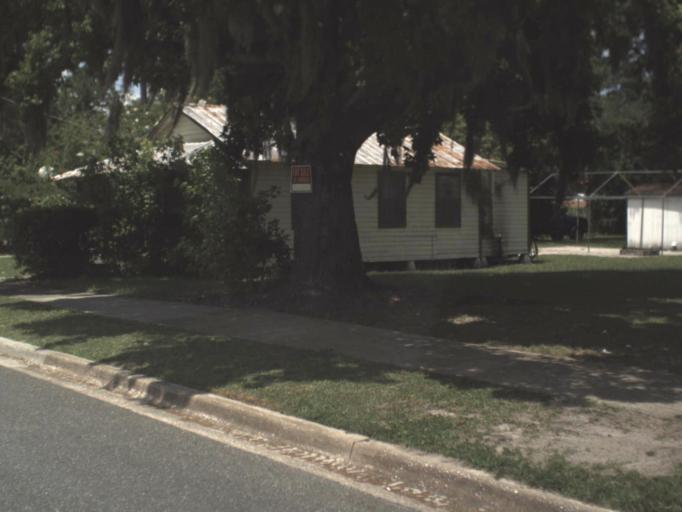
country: US
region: Florida
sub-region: Baker County
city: Macclenny
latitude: 30.2884
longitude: -82.1250
